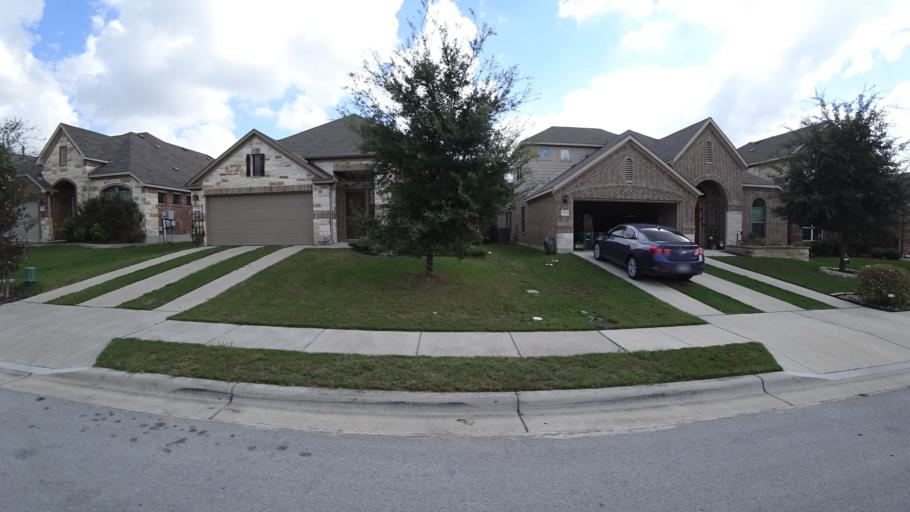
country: US
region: Texas
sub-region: Travis County
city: Onion Creek
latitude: 30.1879
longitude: -97.7986
